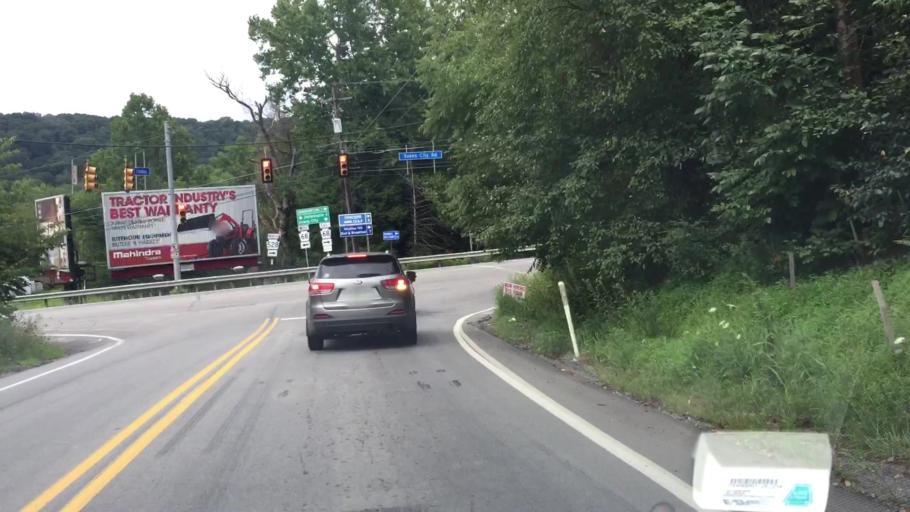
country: US
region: Pennsylvania
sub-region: Butler County
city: Evans City
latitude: 40.7727
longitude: -80.0751
